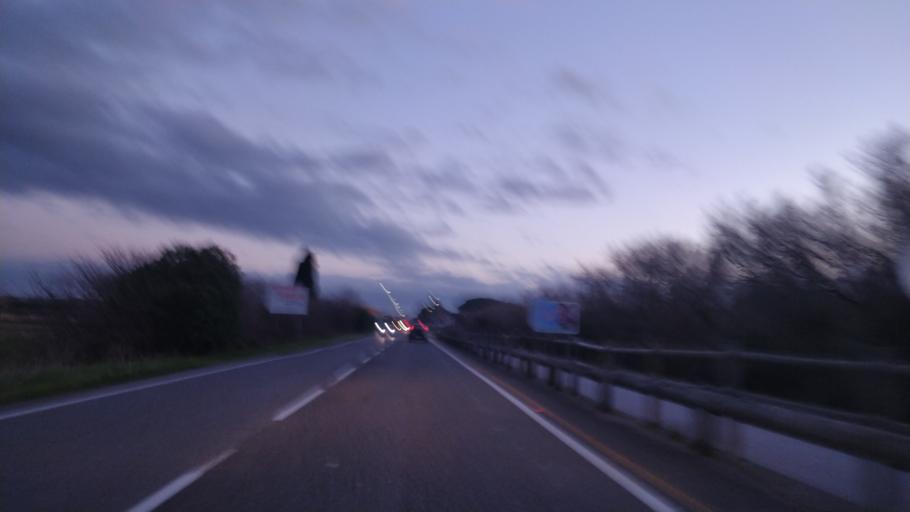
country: IT
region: Tuscany
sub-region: Provincia di Livorno
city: Vada
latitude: 43.3605
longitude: 10.4535
